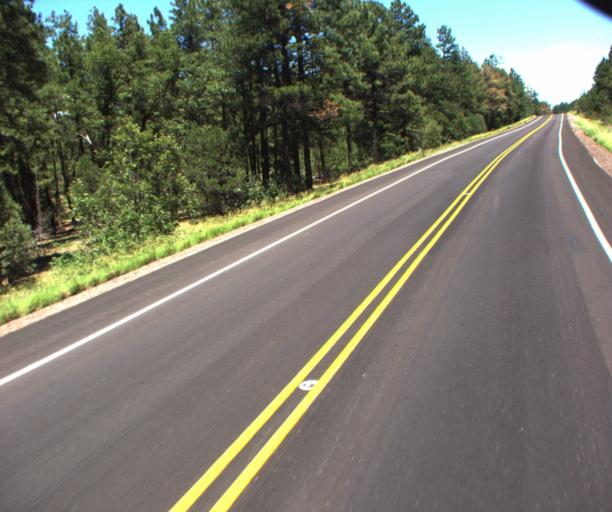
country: US
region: Arizona
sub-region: Navajo County
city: Show Low
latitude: 34.1944
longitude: -110.0897
